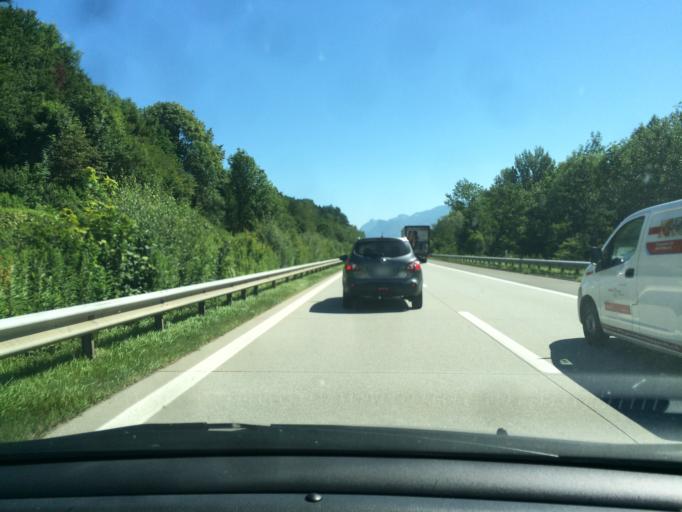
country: CH
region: Saint Gallen
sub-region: Wahlkreis Rheintal
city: Ruthi
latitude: 47.2764
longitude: 9.5352
